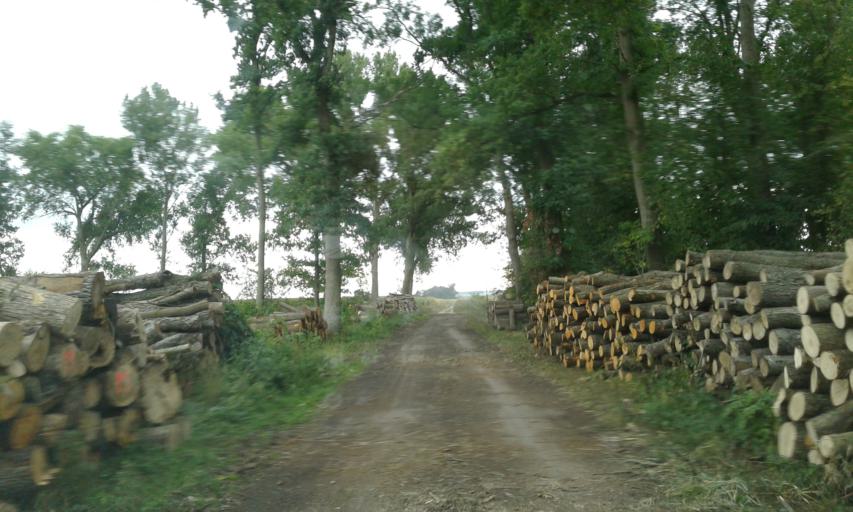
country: PL
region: West Pomeranian Voivodeship
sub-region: Powiat pyrzycki
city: Warnice
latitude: 53.1761
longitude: 14.9959
